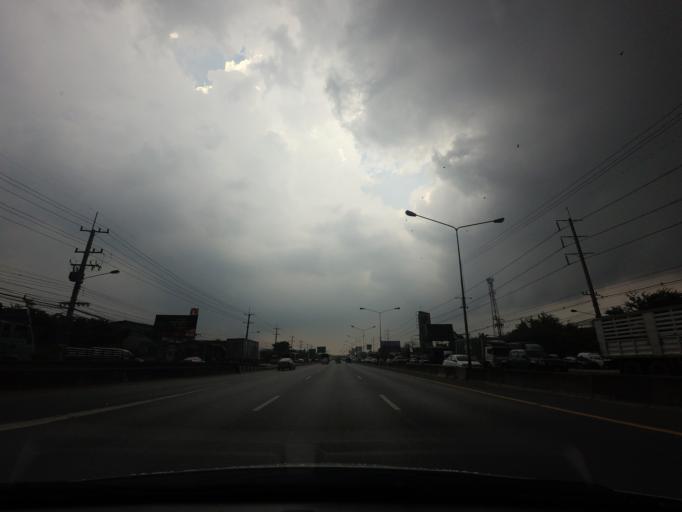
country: TH
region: Nakhon Pathom
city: Salaya
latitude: 13.7862
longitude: 100.2849
